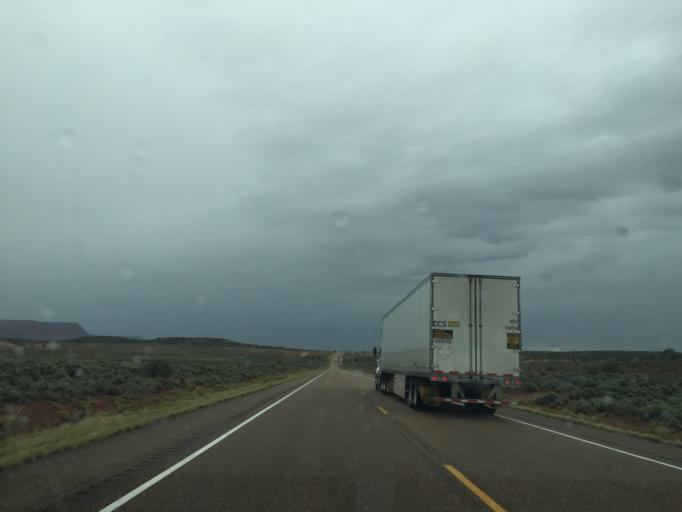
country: US
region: Utah
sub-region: Kane County
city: Kanab
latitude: 37.1271
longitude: -112.0949
